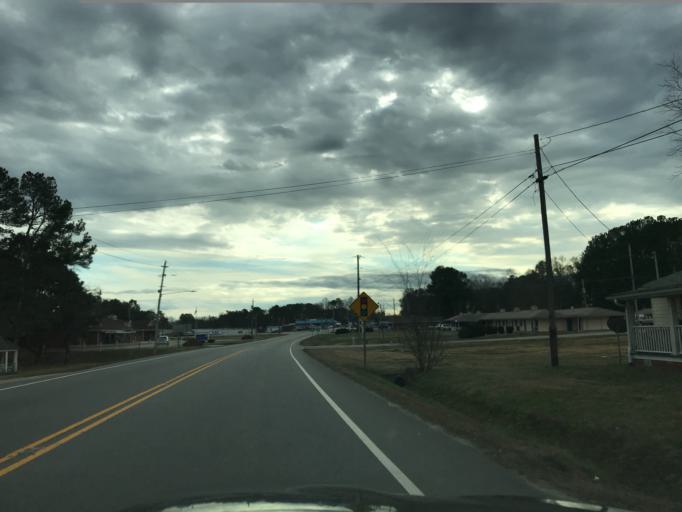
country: US
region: North Carolina
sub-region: Franklin County
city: Louisburg
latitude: 36.1086
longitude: -78.2917
